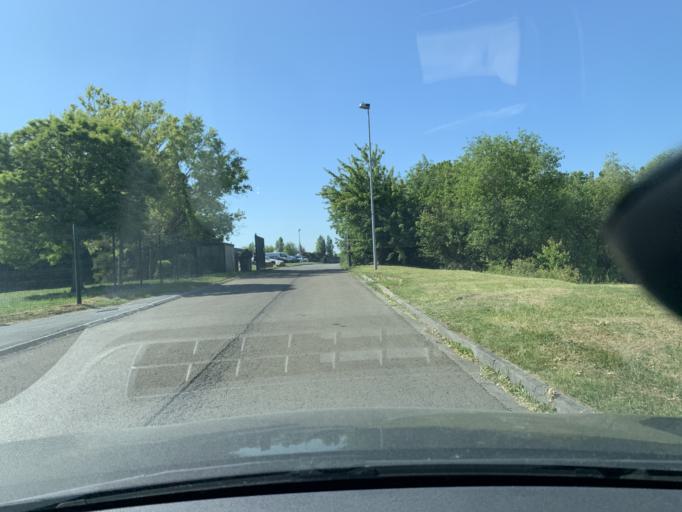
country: FR
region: Nord-Pas-de-Calais
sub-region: Departement du Nord
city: Rumilly-en-Cambresis
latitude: 50.1466
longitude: 3.2242
